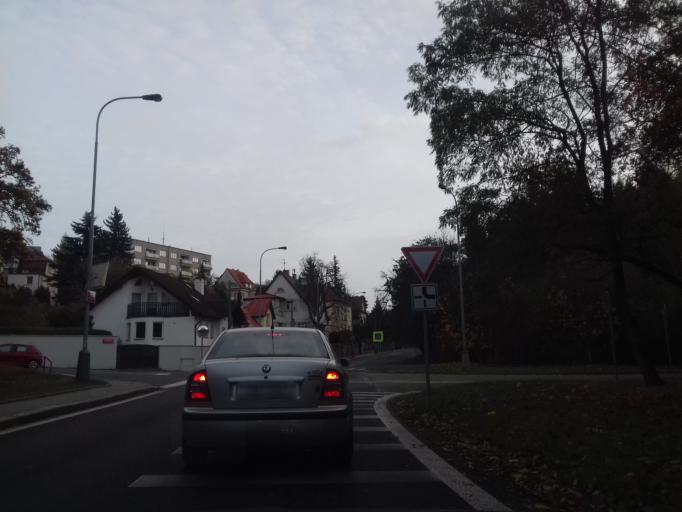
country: CZ
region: Praha
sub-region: Praha 4
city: Hodkovicky
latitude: 50.0268
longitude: 14.4161
